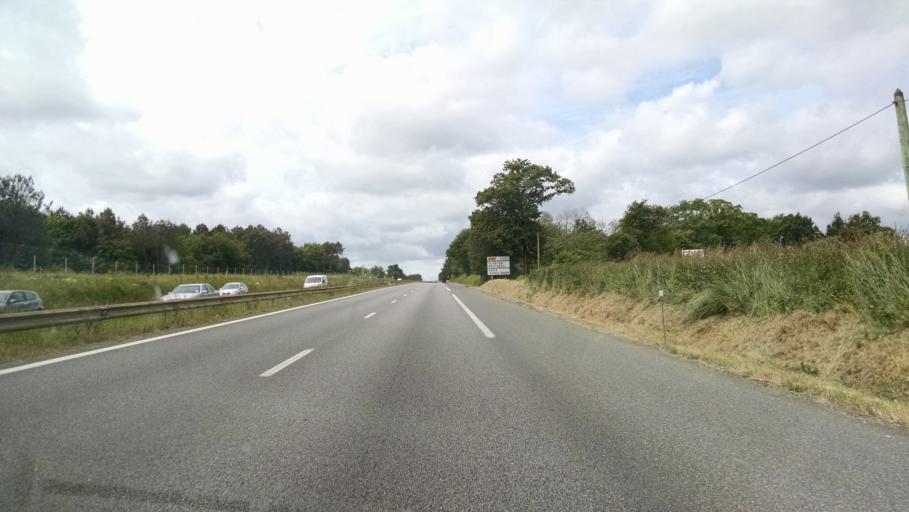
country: FR
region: Brittany
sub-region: Departement du Morbihan
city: Ploeren
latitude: 47.6611
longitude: -2.8465
